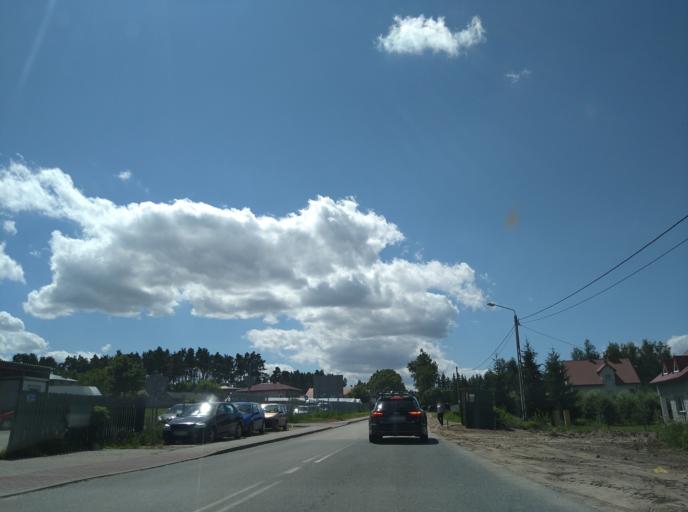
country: PL
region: Masovian Voivodeship
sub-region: Powiat bialobrzeski
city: Promna
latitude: 51.6744
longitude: 20.9419
